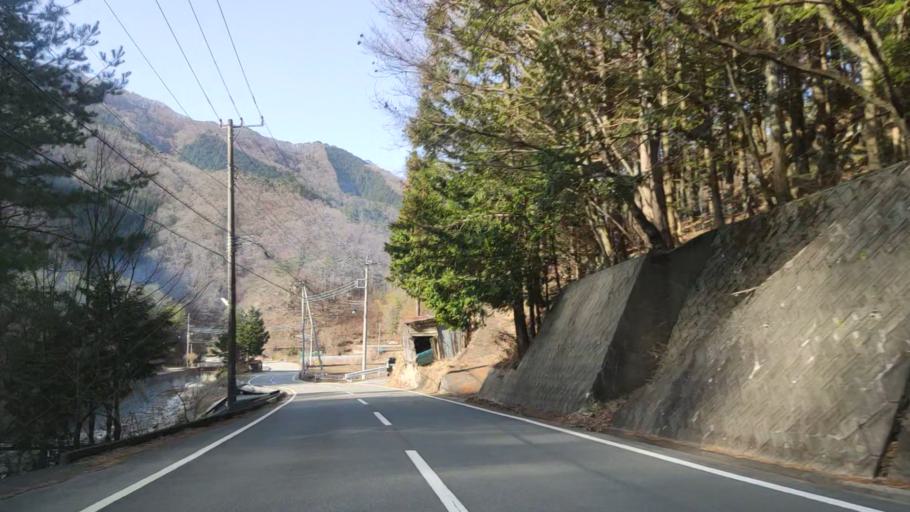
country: JP
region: Yamanashi
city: Fujikawaguchiko
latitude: 35.5518
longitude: 138.6611
